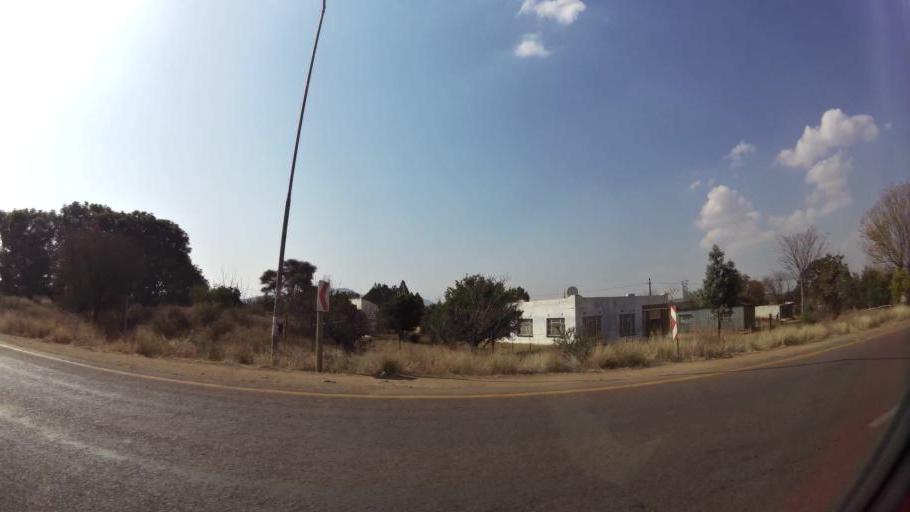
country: ZA
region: North-West
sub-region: Bojanala Platinum District Municipality
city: Mogwase
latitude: -25.3831
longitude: 27.0669
